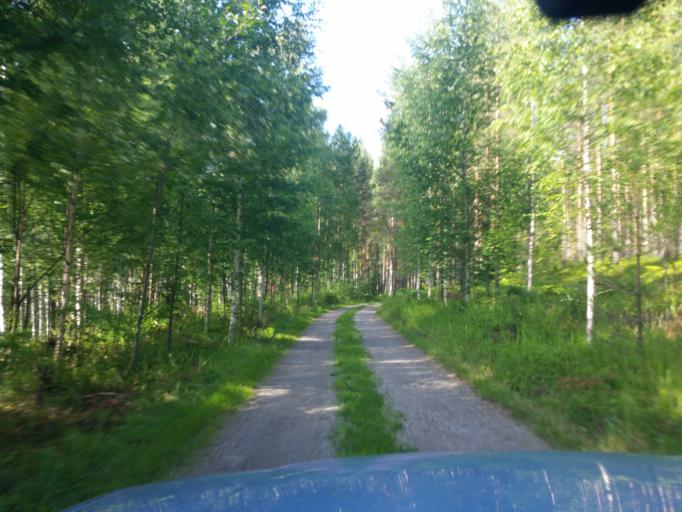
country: FI
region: Southern Savonia
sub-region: Savonlinna
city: Sulkava
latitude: 61.6676
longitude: 28.2766
